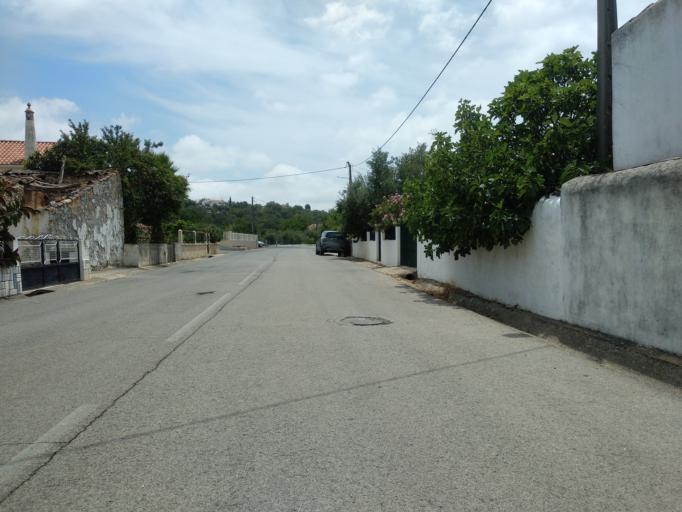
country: PT
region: Faro
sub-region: Sao Bras de Alportel
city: Sao Bras de Alportel
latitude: 37.1687
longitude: -7.8907
